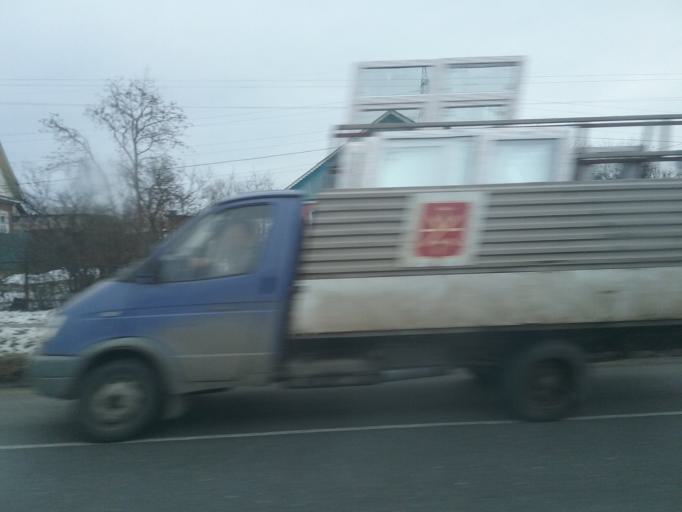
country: RU
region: Tula
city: Skuratovskiy
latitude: 54.1353
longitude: 37.6778
